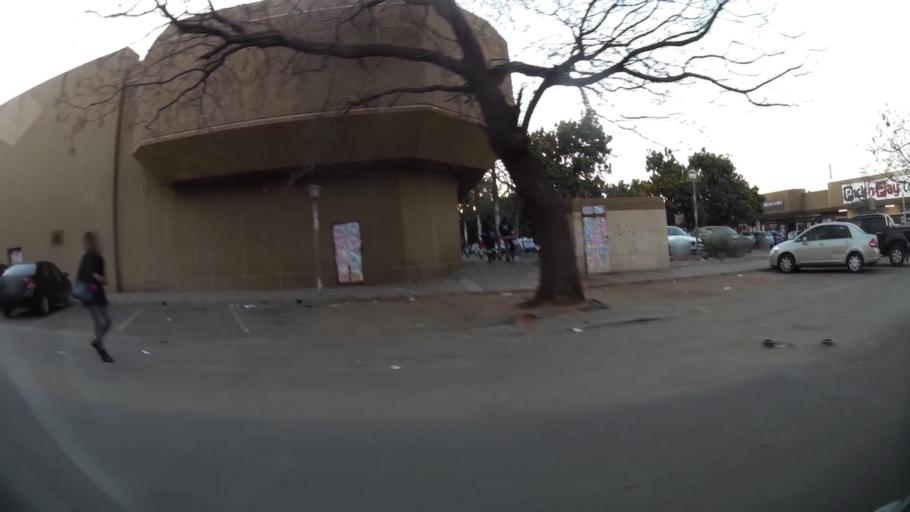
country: ZA
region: North-West
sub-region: Bojanala Platinum District Municipality
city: Rustenburg
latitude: -25.6680
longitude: 27.2426
